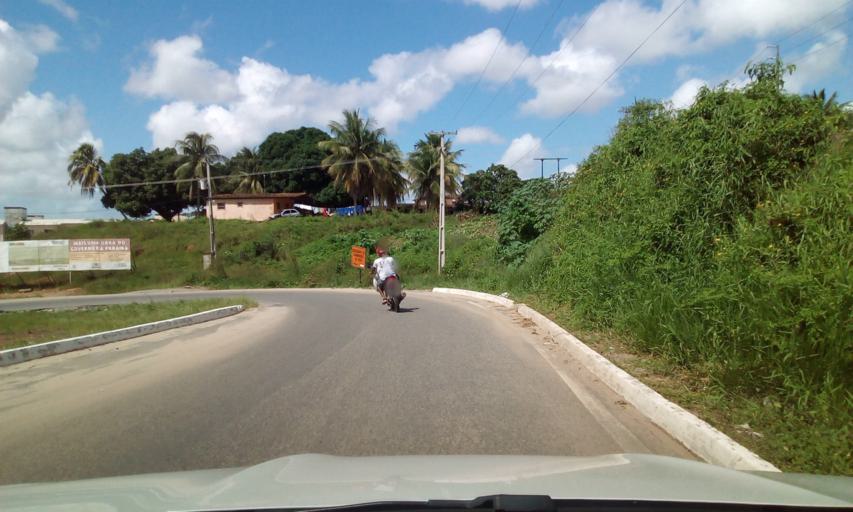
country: BR
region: Paraiba
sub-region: Bayeux
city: Bayeux
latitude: -7.1268
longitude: -34.9490
